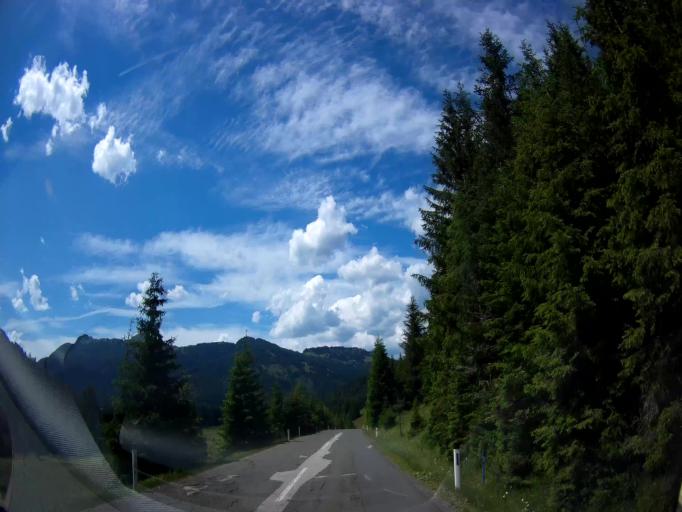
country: AT
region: Styria
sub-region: Politischer Bezirk Murau
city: Stadl an der Mur
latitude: 46.9656
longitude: 14.0205
